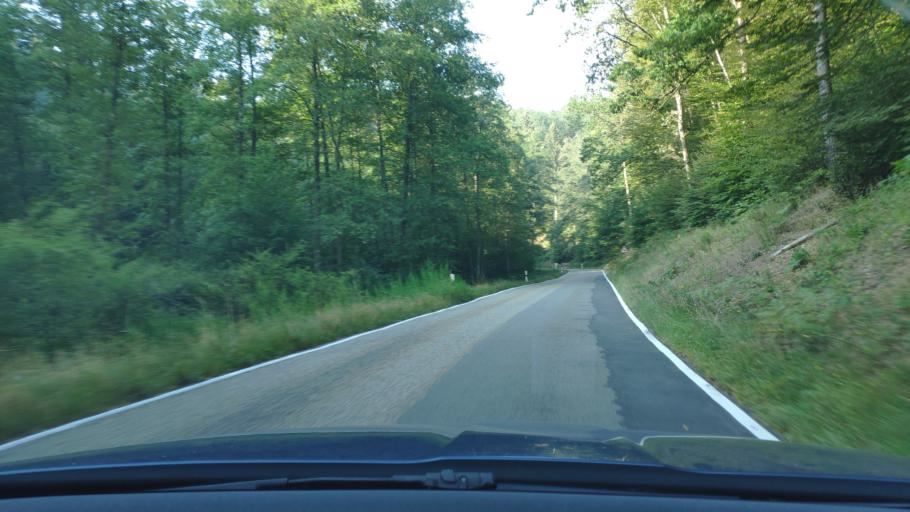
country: DE
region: Rheinland-Pfalz
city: Ludwigswinkel
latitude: 49.1011
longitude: 7.6274
